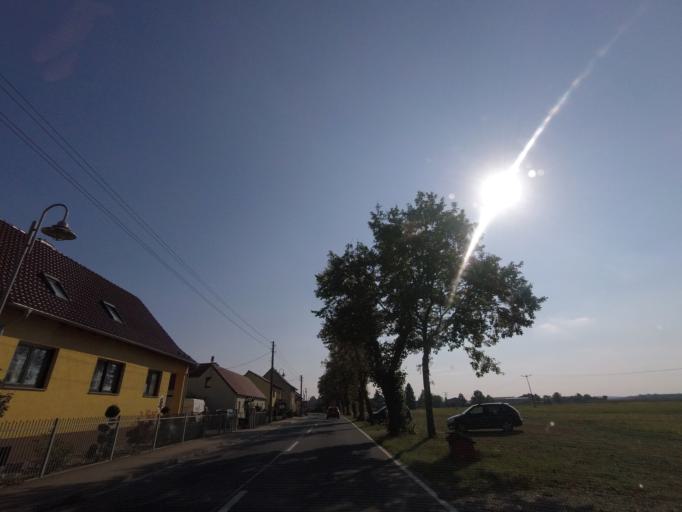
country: DE
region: Saxony-Anhalt
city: Jessen
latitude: 51.8552
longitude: 13.0250
